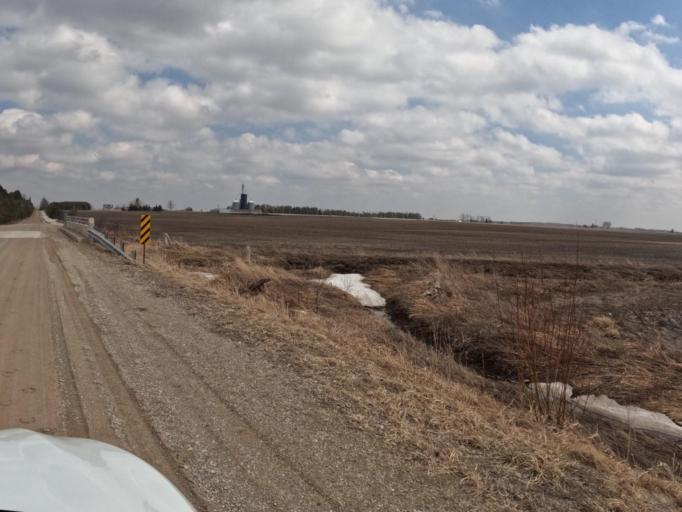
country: CA
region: Ontario
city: Shelburne
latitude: 44.0286
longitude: -80.2505
